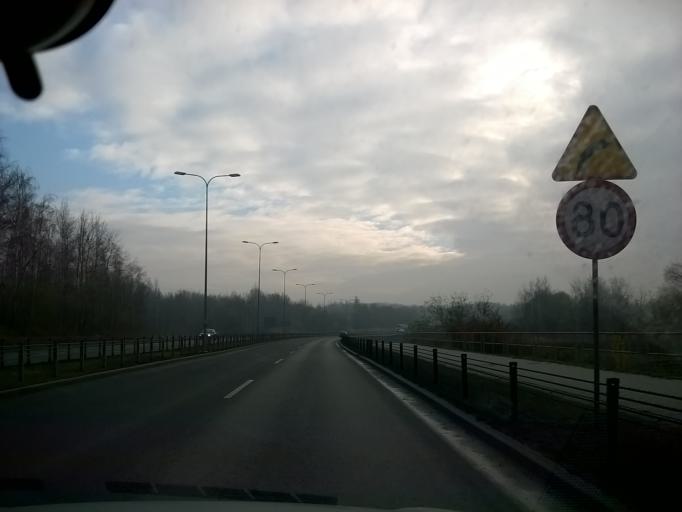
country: PL
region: Silesian Voivodeship
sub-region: Ruda Slaska
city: Ruda Slaska
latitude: 50.2972
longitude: 18.8587
